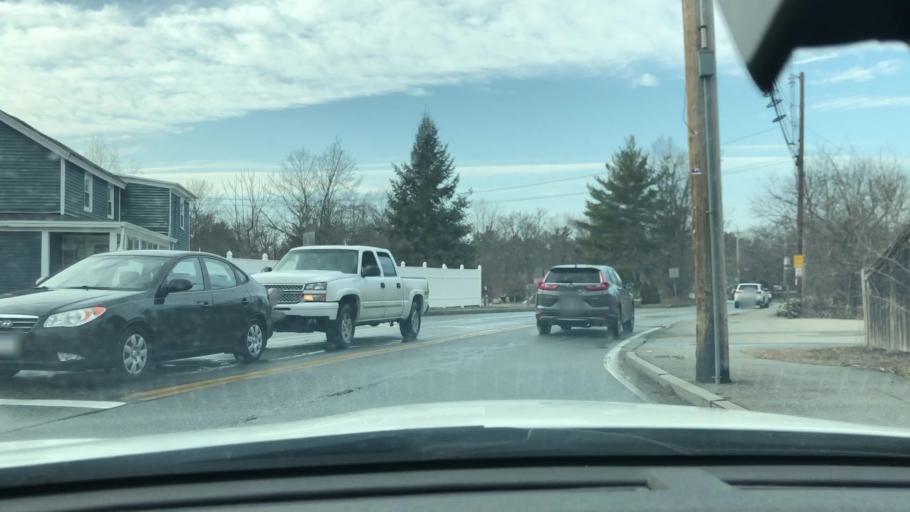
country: US
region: Massachusetts
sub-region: Middlesex County
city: Chelmsford
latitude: 42.5997
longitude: -71.3408
